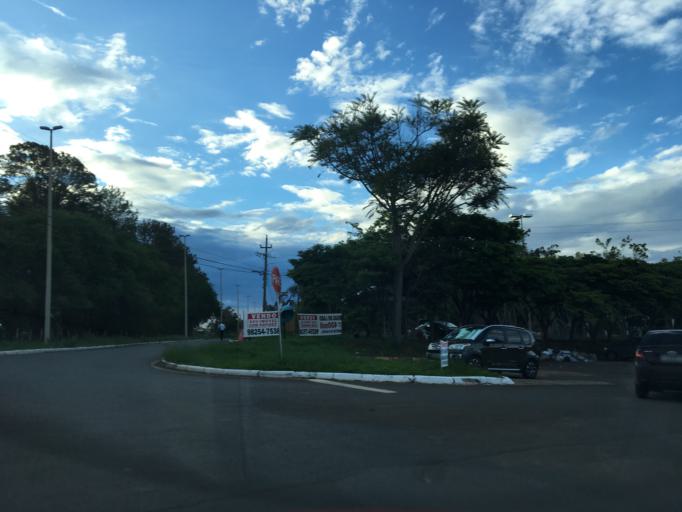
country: BR
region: Federal District
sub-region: Brasilia
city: Brasilia
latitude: -15.8061
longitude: -47.8312
